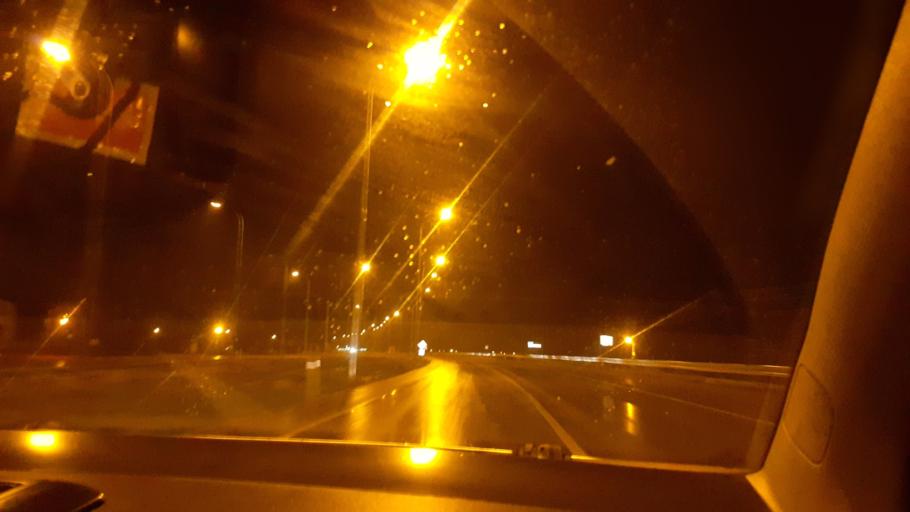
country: TR
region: Hatay
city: Aktepe
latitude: 36.7219
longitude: 36.5165
